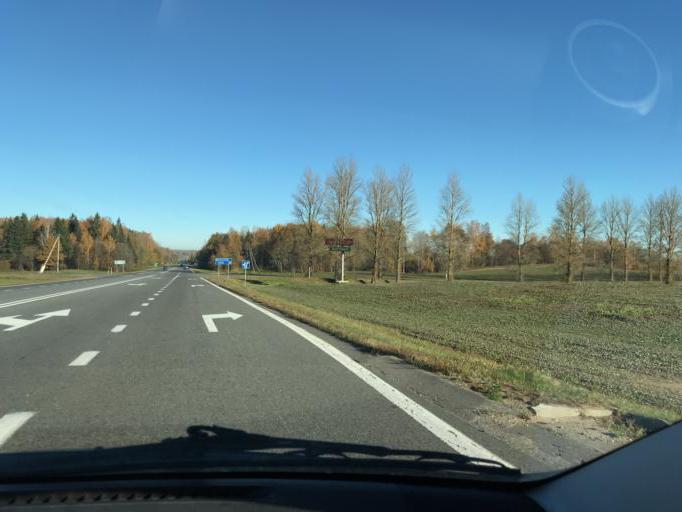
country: BY
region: Vitebsk
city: Vitebsk
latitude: 55.0498
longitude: 30.3131
